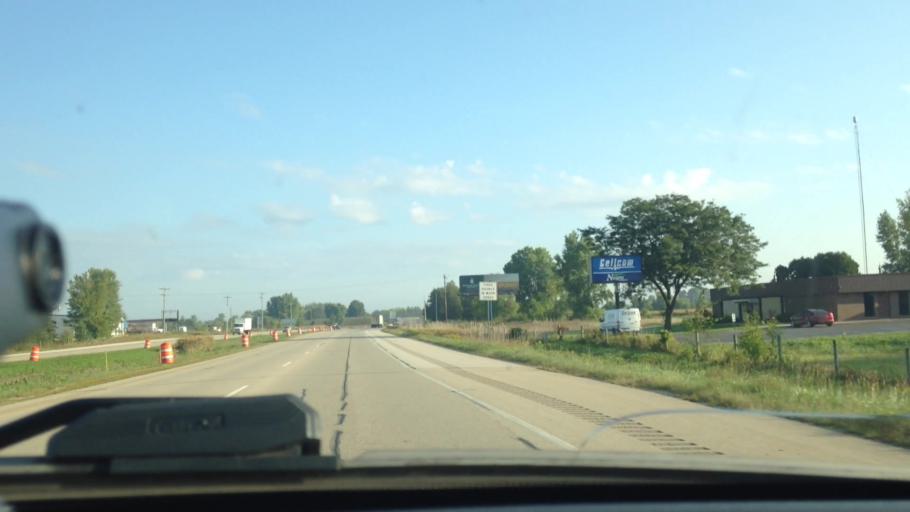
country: US
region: Wisconsin
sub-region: Oconto County
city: Oconto Falls
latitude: 44.7714
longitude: -88.0504
